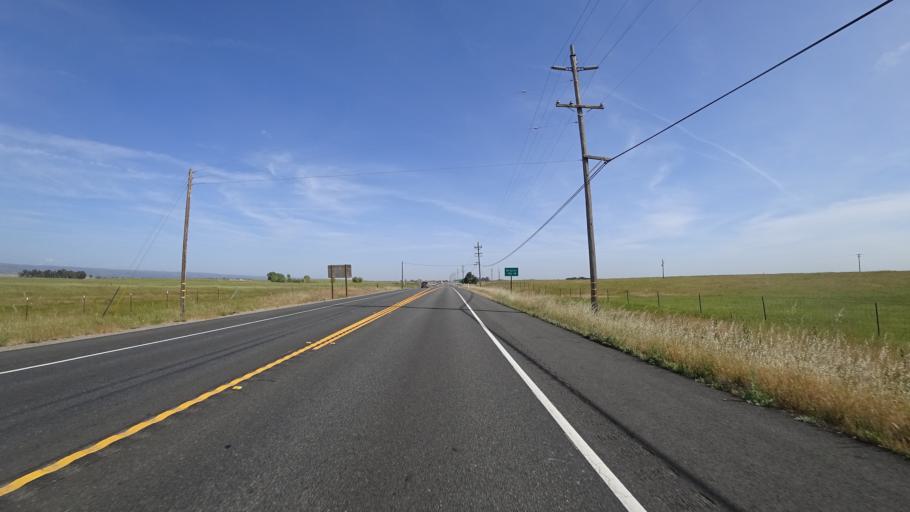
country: US
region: California
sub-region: Glenn County
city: Hamilton City
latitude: 39.8650
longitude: -121.9617
